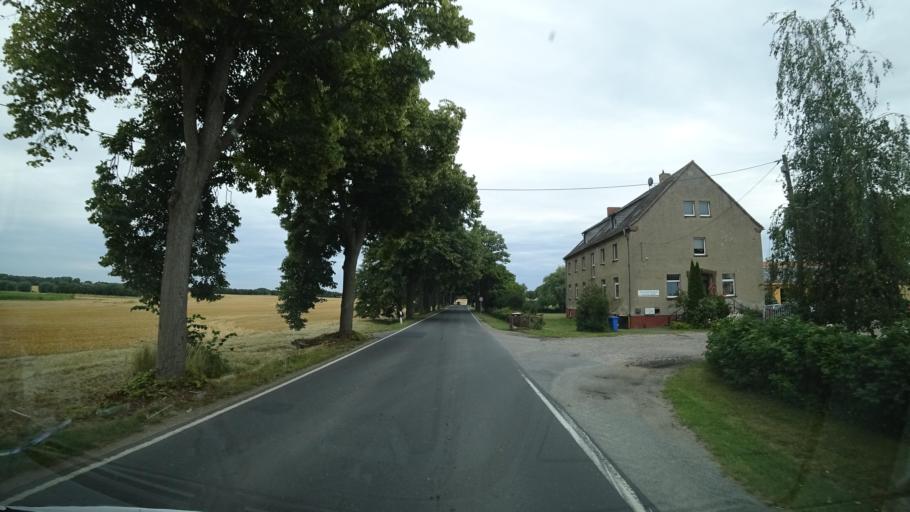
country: DE
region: Mecklenburg-Vorpommern
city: Poseritz
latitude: 54.3062
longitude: 13.2256
